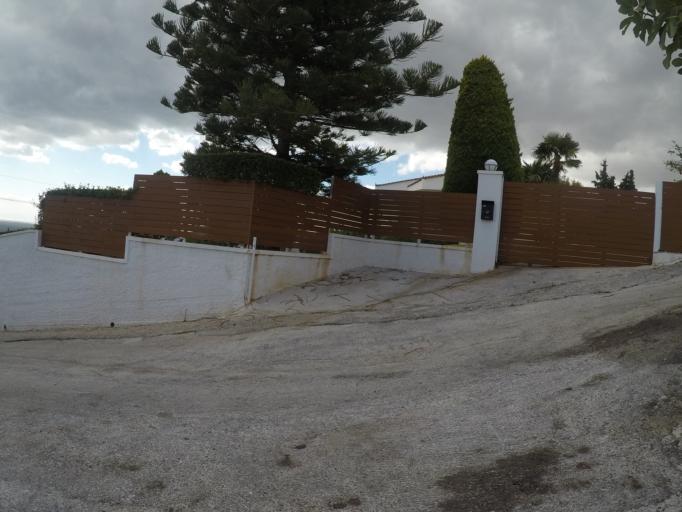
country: GR
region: Attica
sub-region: Nomarchia Anatolikis Attikis
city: Agios Dimitrios Kropias
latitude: 37.8071
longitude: 23.8570
